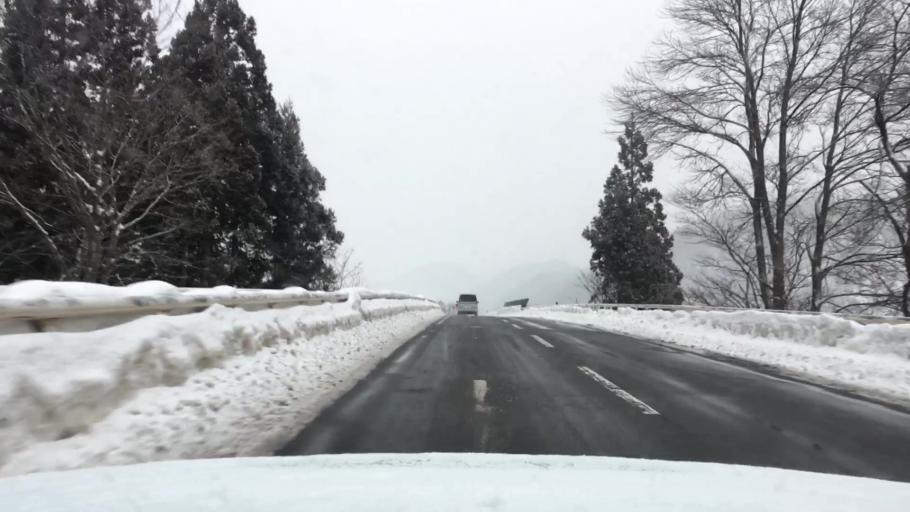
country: JP
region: Akita
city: Hanawa
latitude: 40.0621
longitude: 141.0144
